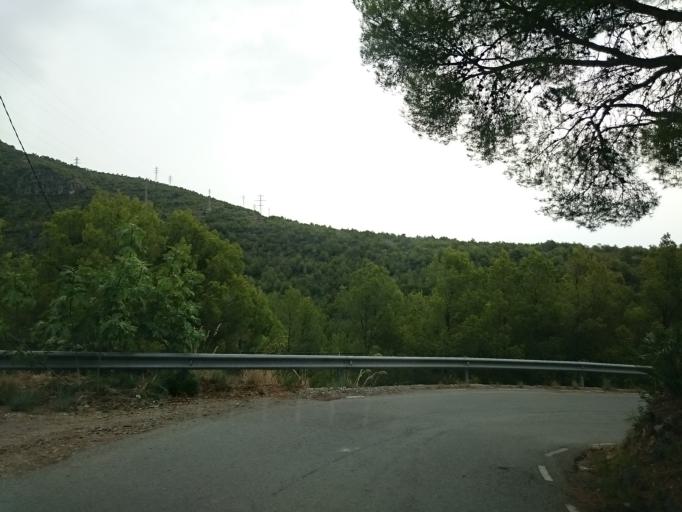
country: ES
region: Catalonia
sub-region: Provincia de Barcelona
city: Castelldefels
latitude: 41.2679
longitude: 1.9280
